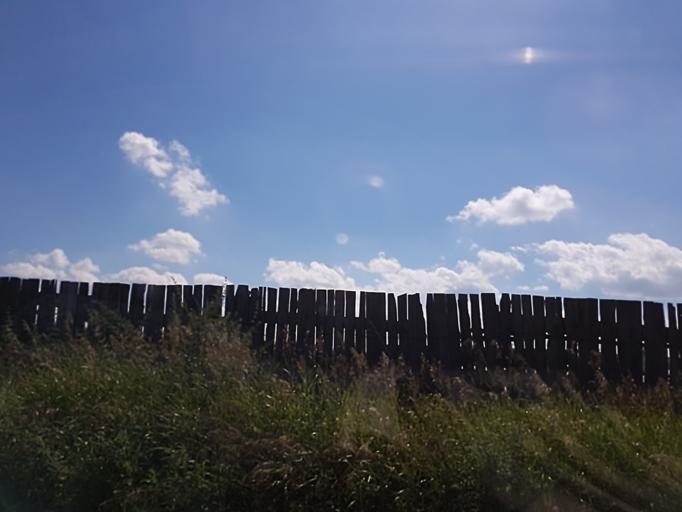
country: RU
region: Irkutsk
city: Kitoy
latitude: 52.6044
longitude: 103.8378
